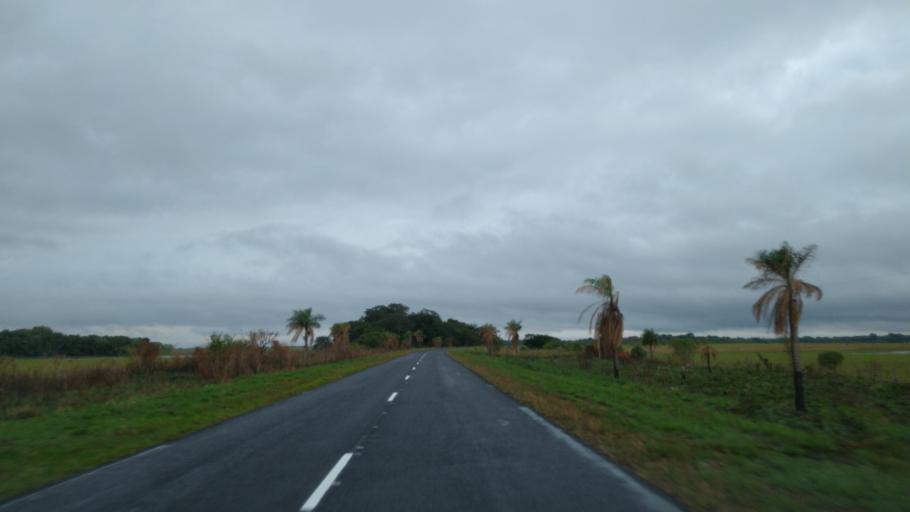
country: AR
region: Corrientes
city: Loreto
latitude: -27.6916
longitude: -57.2179
